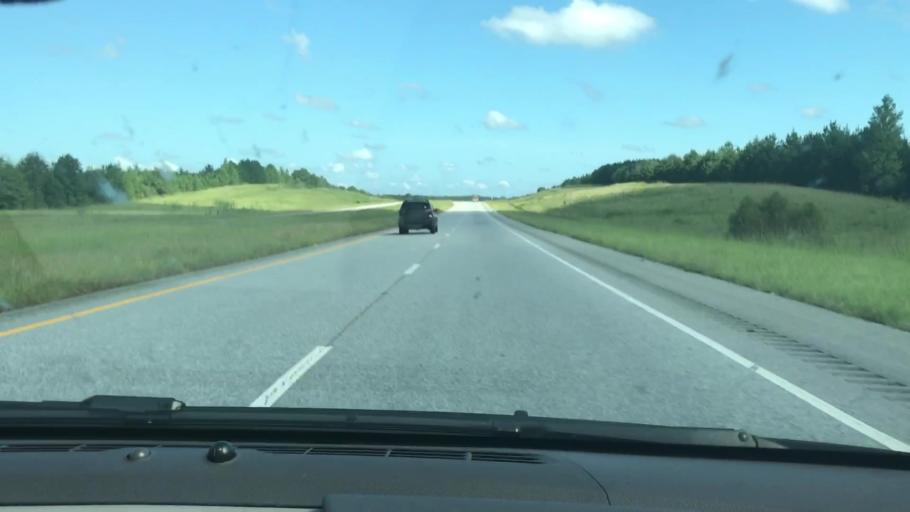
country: US
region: Alabama
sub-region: Barbour County
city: Eufaula
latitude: 32.1730
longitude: -85.1764
